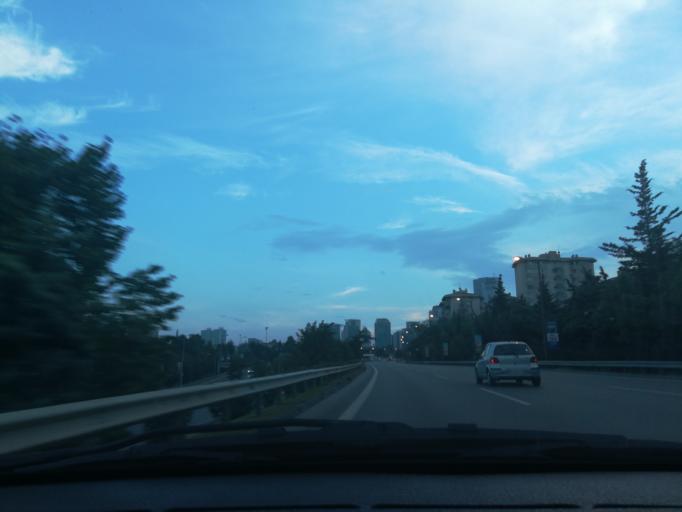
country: TR
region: Istanbul
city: Sisli
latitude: 41.0920
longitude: 29.0206
